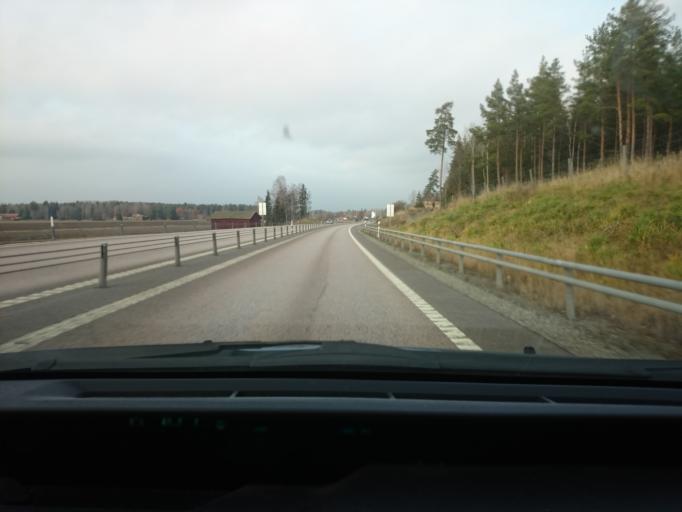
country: SE
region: Vaestmanland
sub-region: Sala Kommun
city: Sala
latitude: 59.9002
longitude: 16.5386
